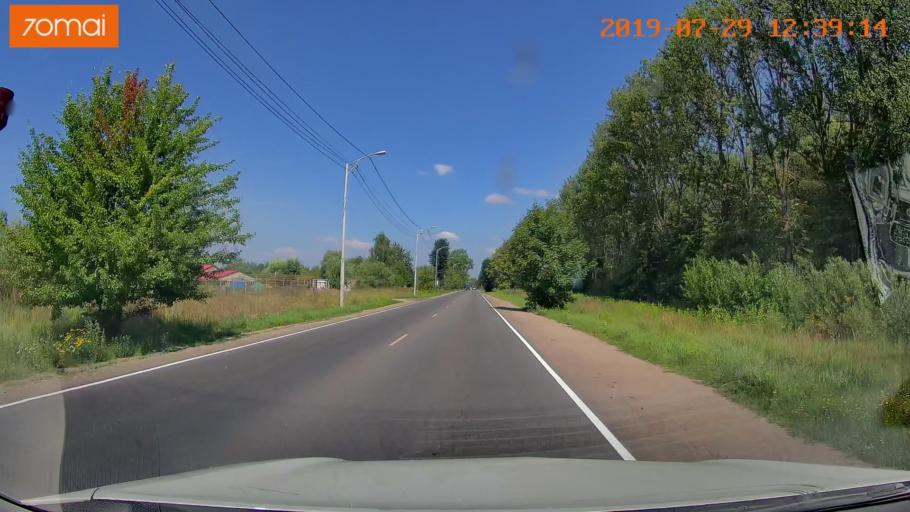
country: RU
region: Kaliningrad
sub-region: Gorod Kaliningrad
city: Kaliningrad
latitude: 54.6578
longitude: 20.5418
